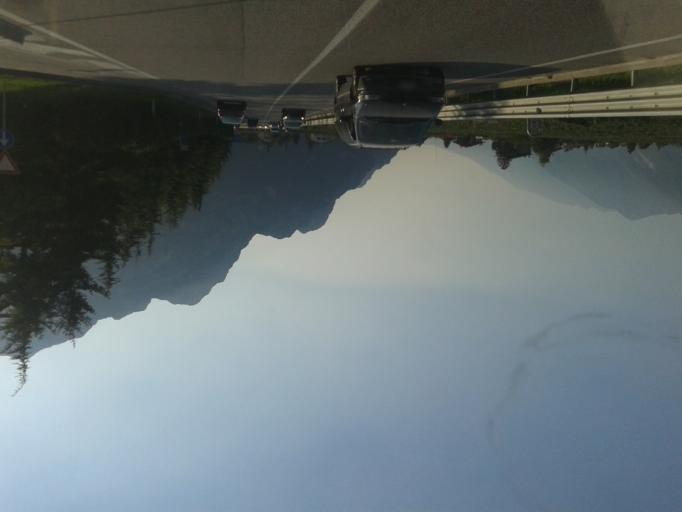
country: IT
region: Trentino-Alto Adige
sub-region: Provincia di Trento
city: Tenno
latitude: 45.9099
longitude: 10.8556
